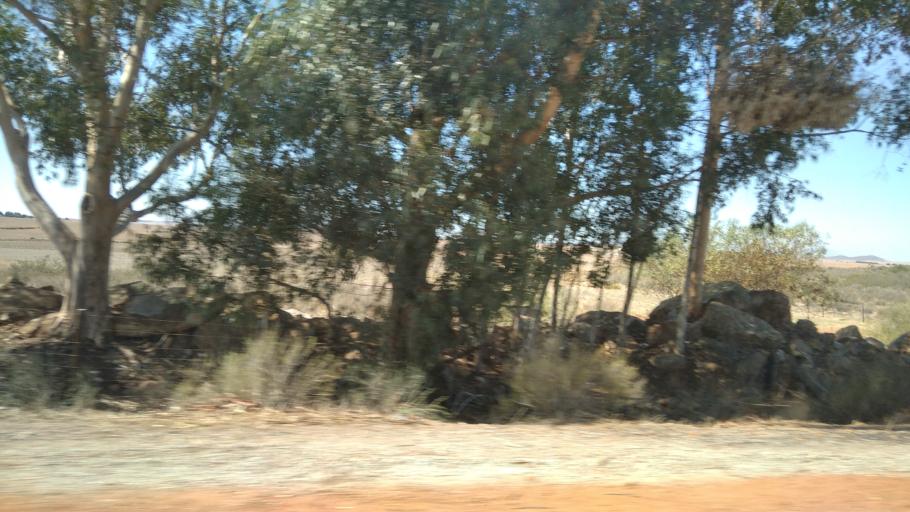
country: ZA
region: Western Cape
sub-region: West Coast District Municipality
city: Moorreesburg
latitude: -33.2506
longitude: 18.5823
